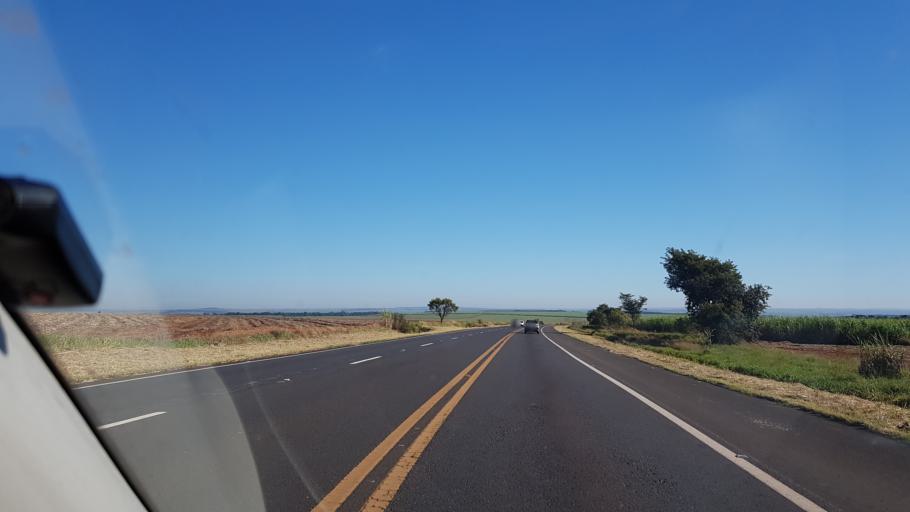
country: BR
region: Sao Paulo
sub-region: Assis
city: Assis
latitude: -22.5707
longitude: -50.5190
